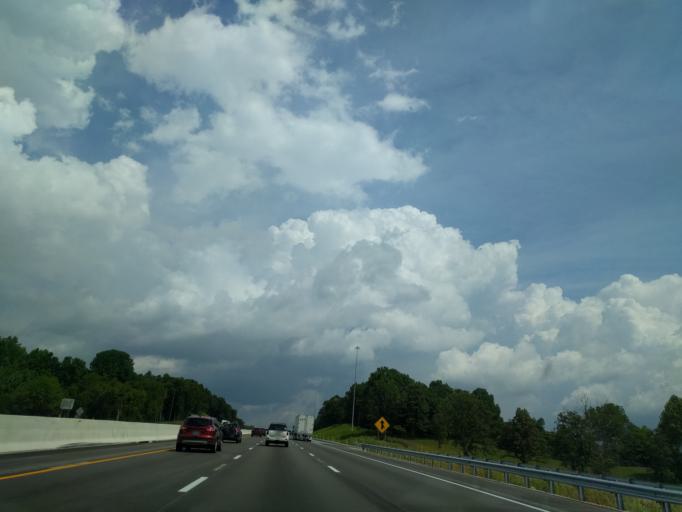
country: US
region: Kentucky
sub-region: Hart County
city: Munfordville
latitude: 37.3824
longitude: -85.8873
